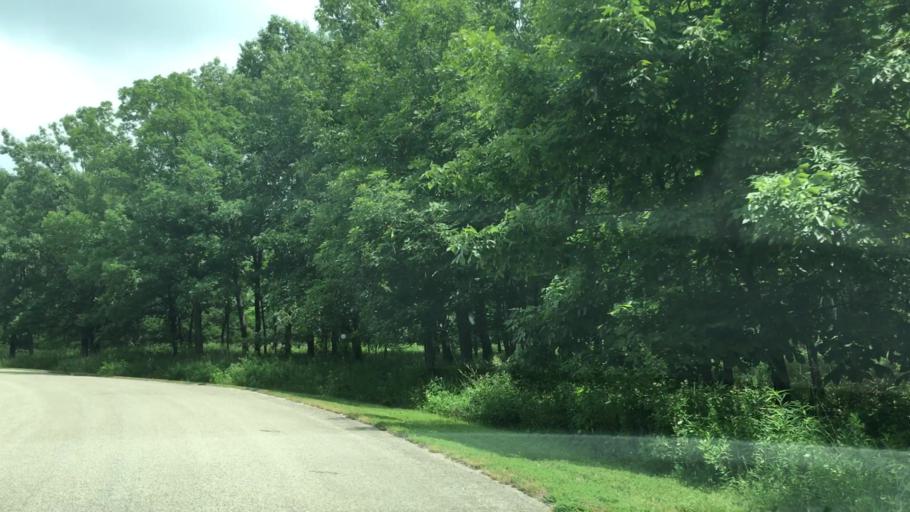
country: US
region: Iowa
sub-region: Johnson County
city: Tiffin
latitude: 41.7369
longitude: -91.7263
